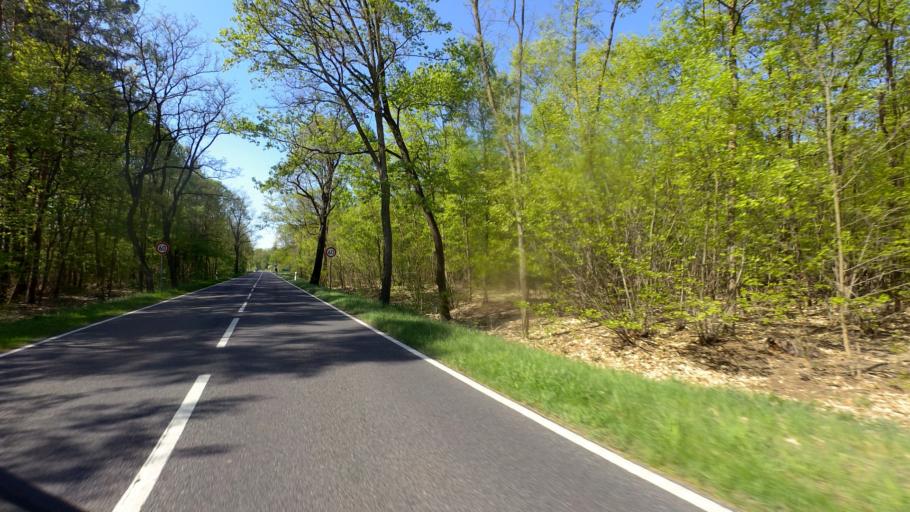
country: DE
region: Brandenburg
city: Gross Koris
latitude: 52.1819
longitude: 13.7087
